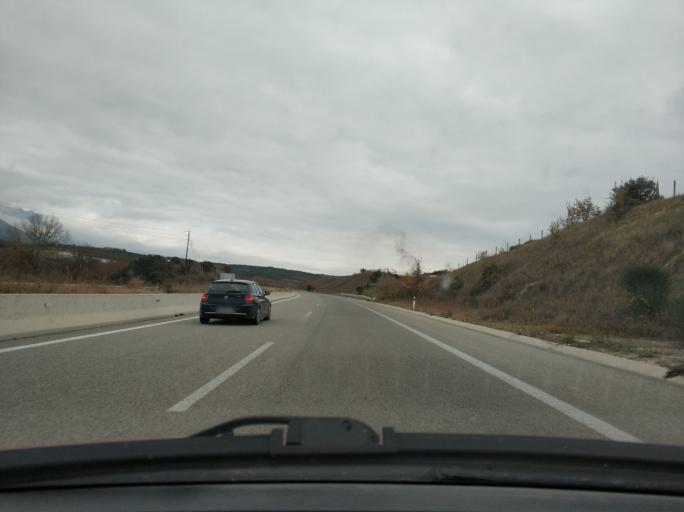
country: GR
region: East Macedonia and Thrace
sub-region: Nomos Kavalas
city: Paralia Ofryniou
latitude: 40.7895
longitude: 23.9707
